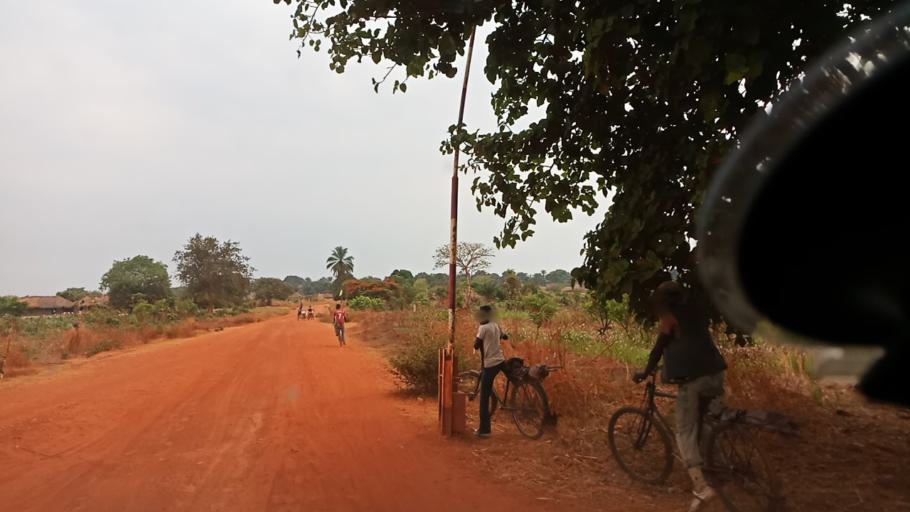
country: ZM
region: Luapula
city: Nchelenge
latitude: -9.1067
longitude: 28.3017
